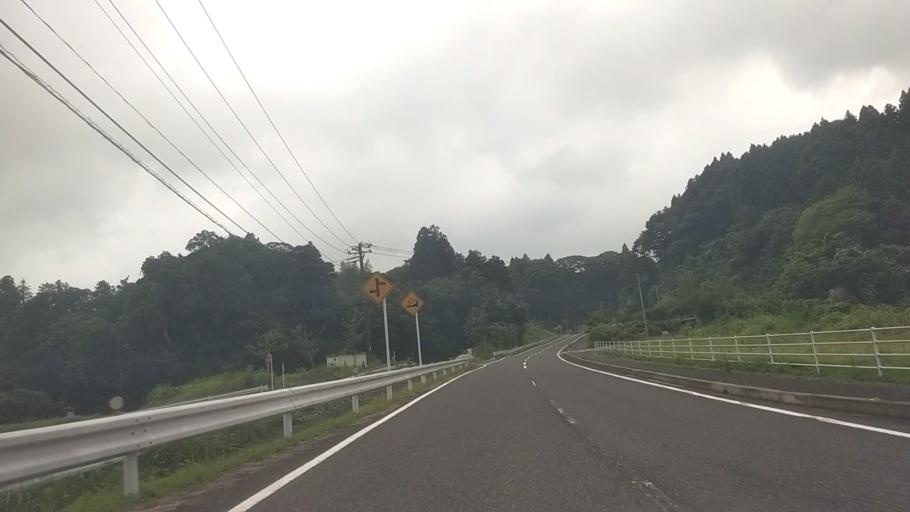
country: JP
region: Chiba
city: Kawaguchi
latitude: 35.2277
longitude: 140.1527
